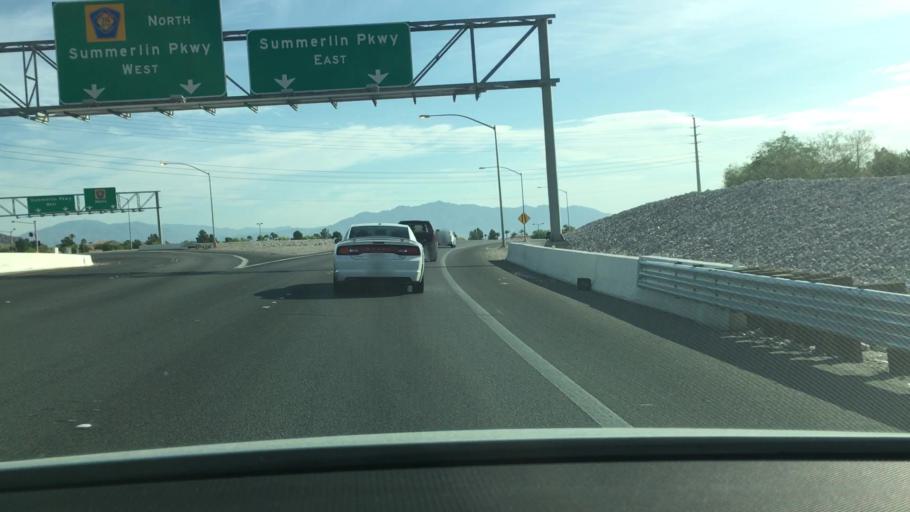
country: US
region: Nevada
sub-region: Clark County
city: Summerlin South
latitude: 36.1891
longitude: -115.3419
